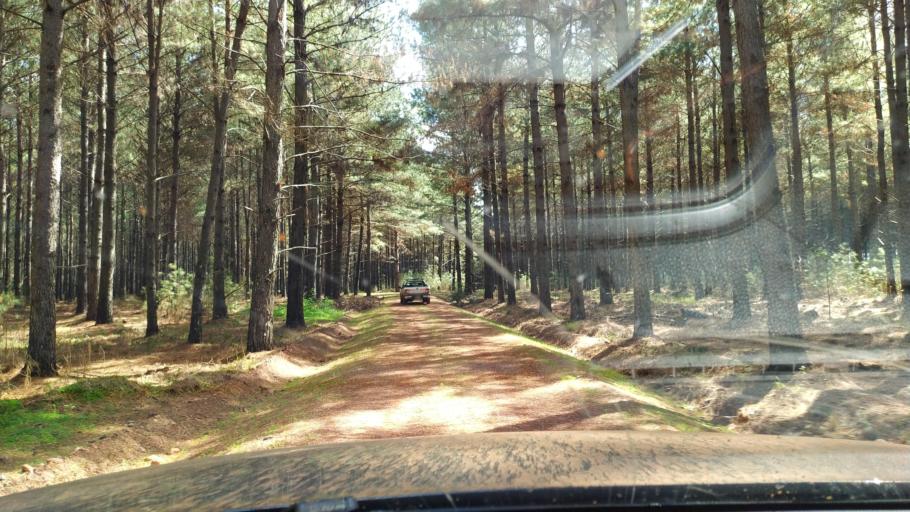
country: AR
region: Corrientes
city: Santo Tome
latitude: -28.4645
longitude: -55.9935
